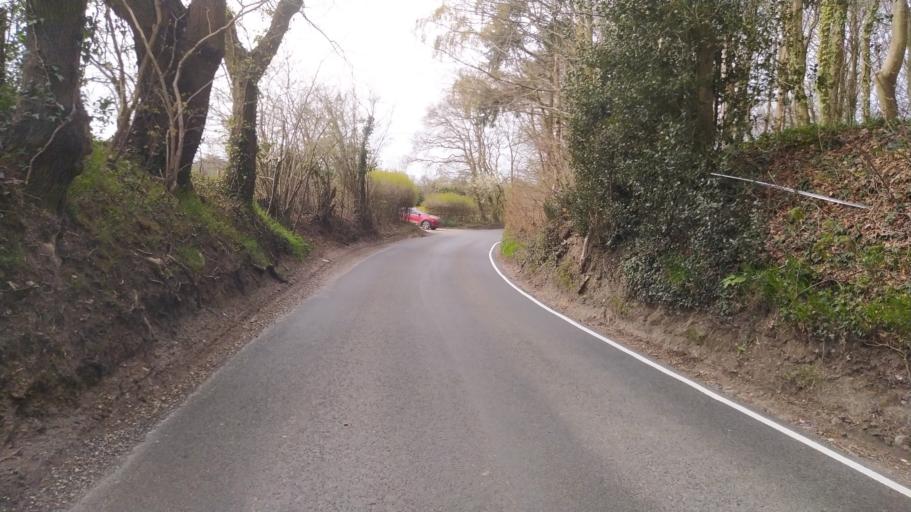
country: GB
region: England
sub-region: Hampshire
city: Wickham
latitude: 50.8930
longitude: -1.2119
